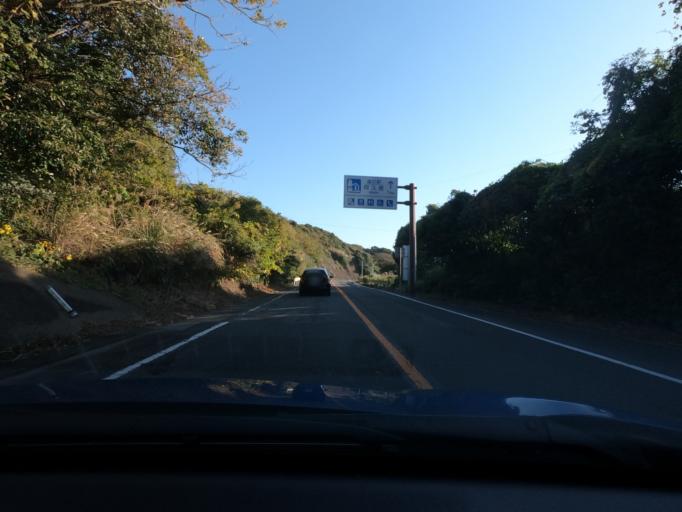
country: JP
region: Kagoshima
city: Akune
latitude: 31.9541
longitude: 130.2162
